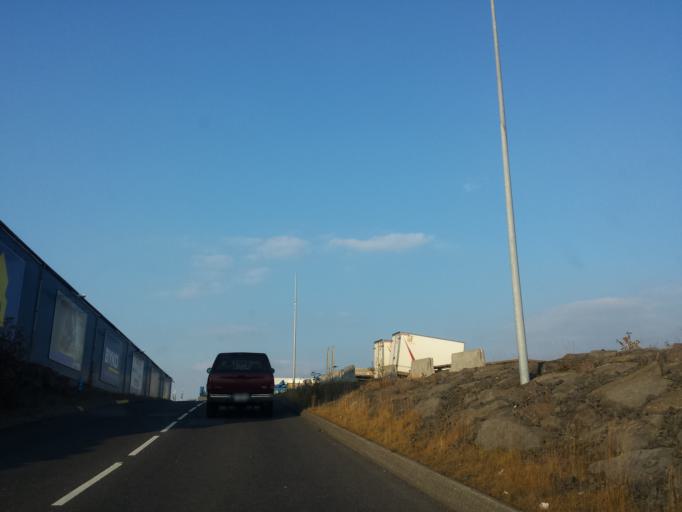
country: IS
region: Capital Region
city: Reykjavik
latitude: 64.1080
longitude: -21.8521
